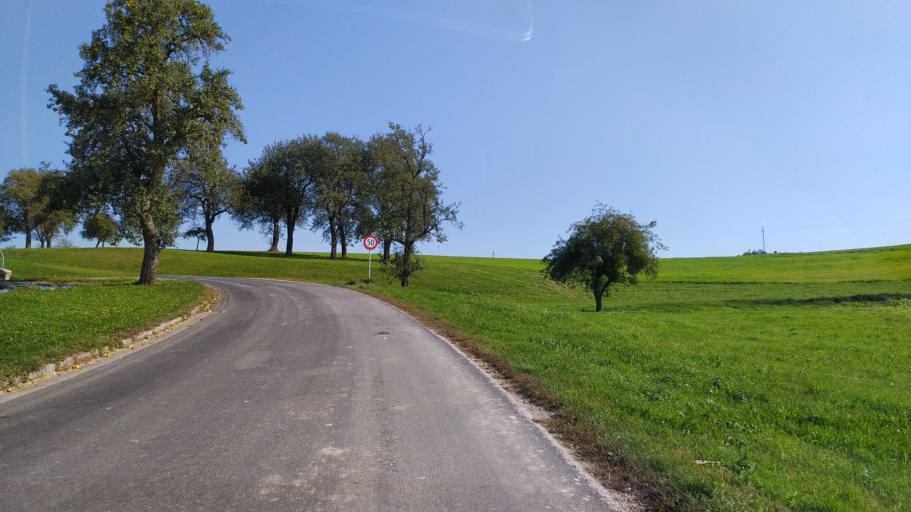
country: AT
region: Lower Austria
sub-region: Politischer Bezirk Amstetten
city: Zeillern
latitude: 48.1142
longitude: 14.7453
